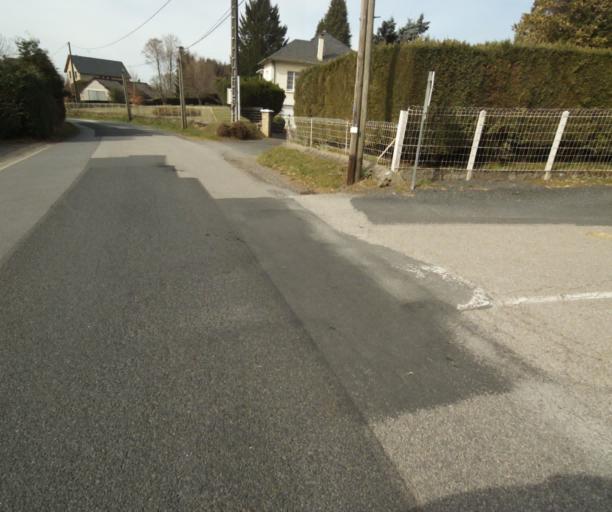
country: FR
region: Limousin
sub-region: Departement de la Correze
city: Correze
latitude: 45.4211
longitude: 1.8313
